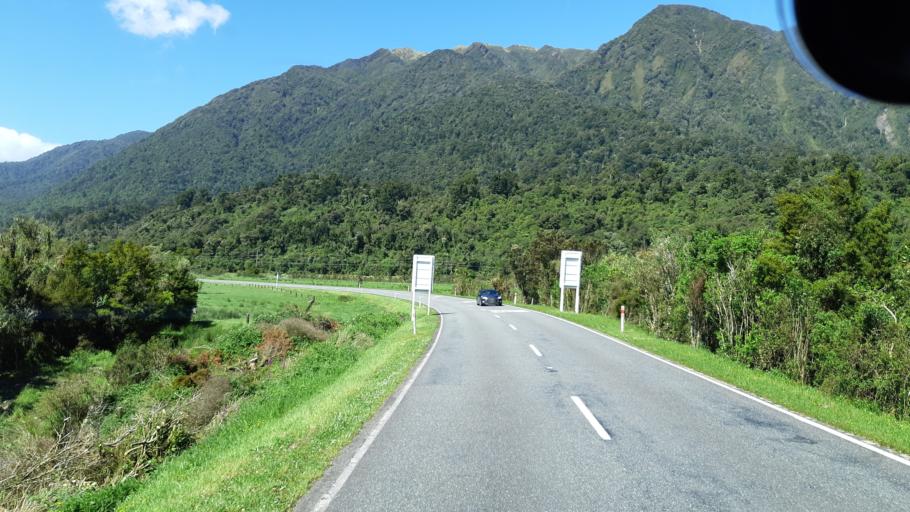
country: NZ
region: West Coast
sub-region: Westland District
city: Hokitika
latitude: -43.1553
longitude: 170.6272
